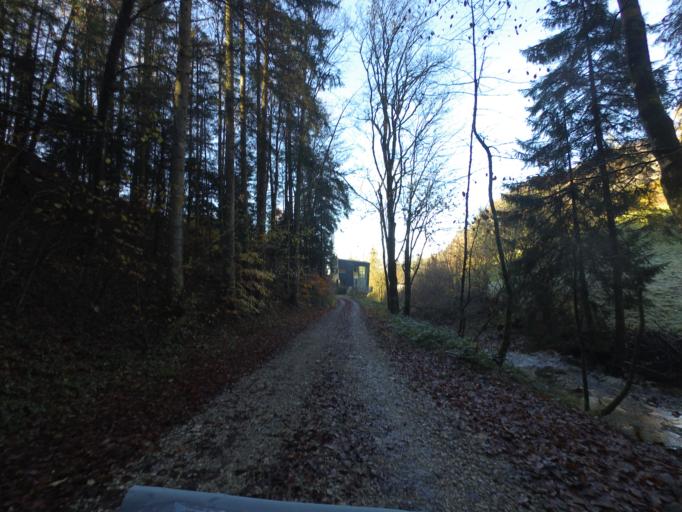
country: AT
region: Salzburg
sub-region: Politischer Bezirk Hallein
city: Adnet
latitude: 47.6865
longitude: 13.1500
